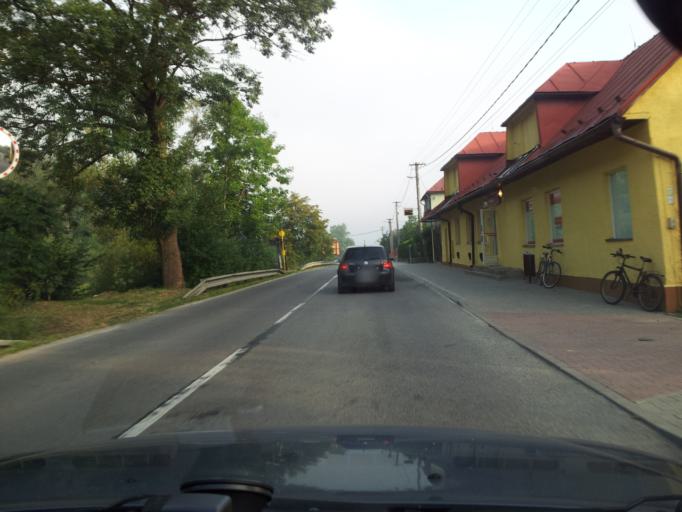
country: SK
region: Zilinsky
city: Cadca
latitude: 49.3741
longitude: 18.8924
